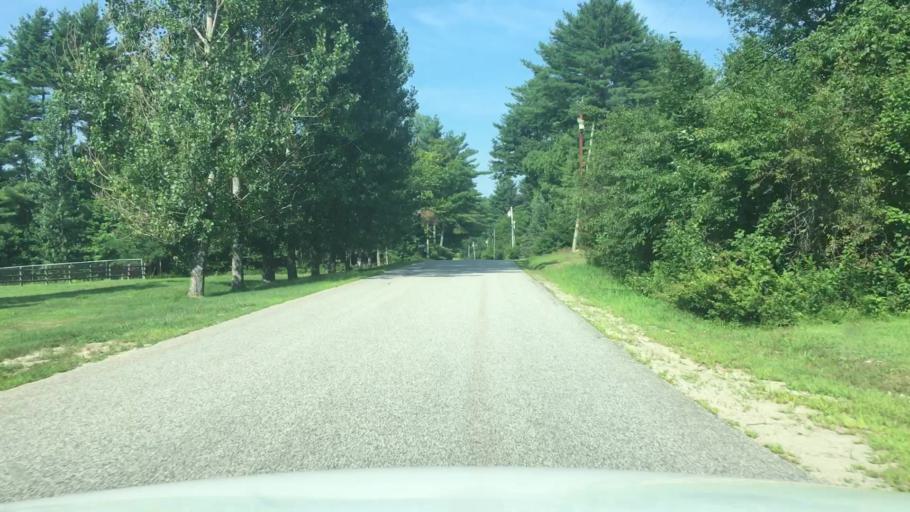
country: US
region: Maine
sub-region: Kennebec County
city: Monmouth
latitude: 44.2428
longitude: -70.0982
